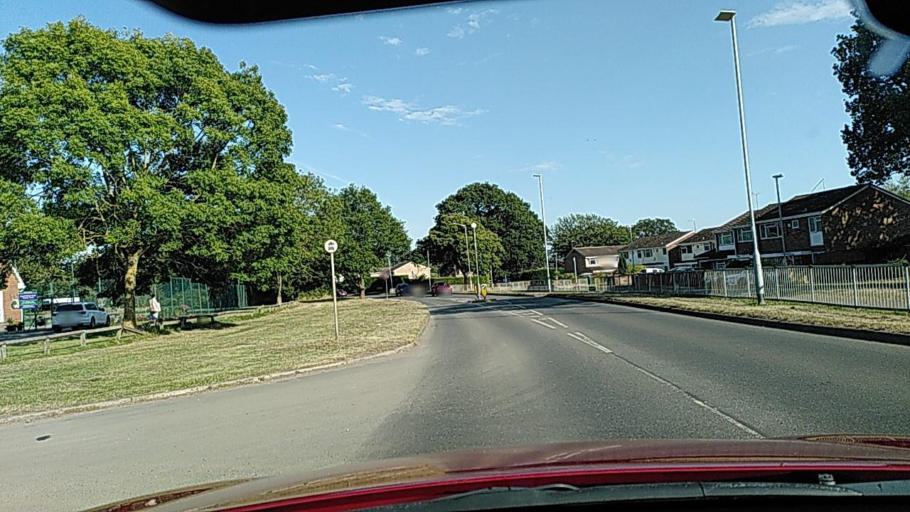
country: GB
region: England
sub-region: Reading
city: Reading
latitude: 51.4850
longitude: -0.9563
